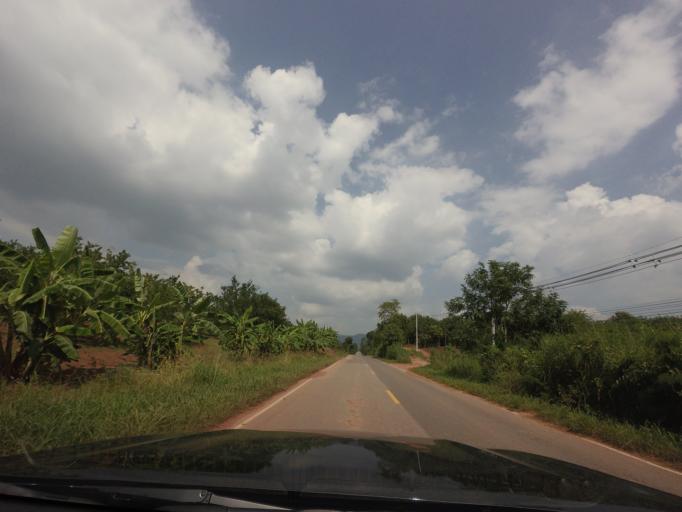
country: TH
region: Uttaradit
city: Ban Khok
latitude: 18.0329
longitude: 101.0888
